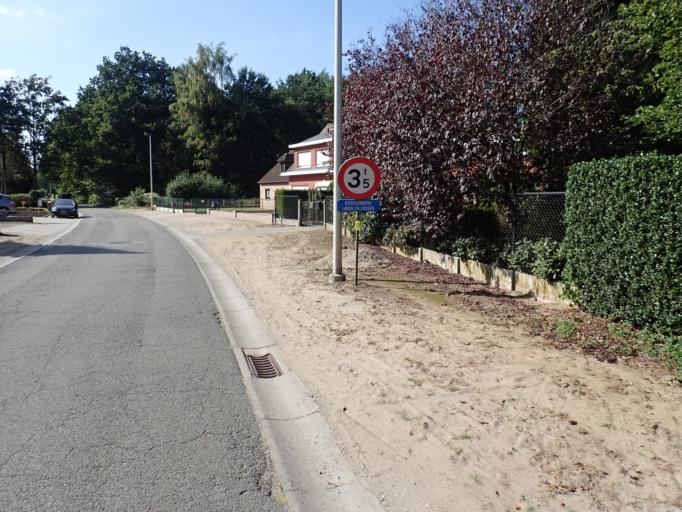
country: BE
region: Flanders
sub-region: Provincie Antwerpen
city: Grobbendonk
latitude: 51.2025
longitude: 4.7340
